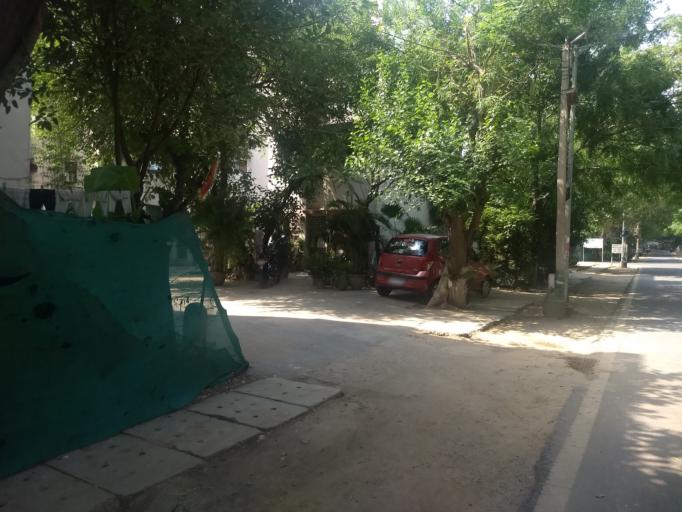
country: IN
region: NCT
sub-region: New Delhi
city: New Delhi
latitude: 28.5590
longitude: 77.2237
